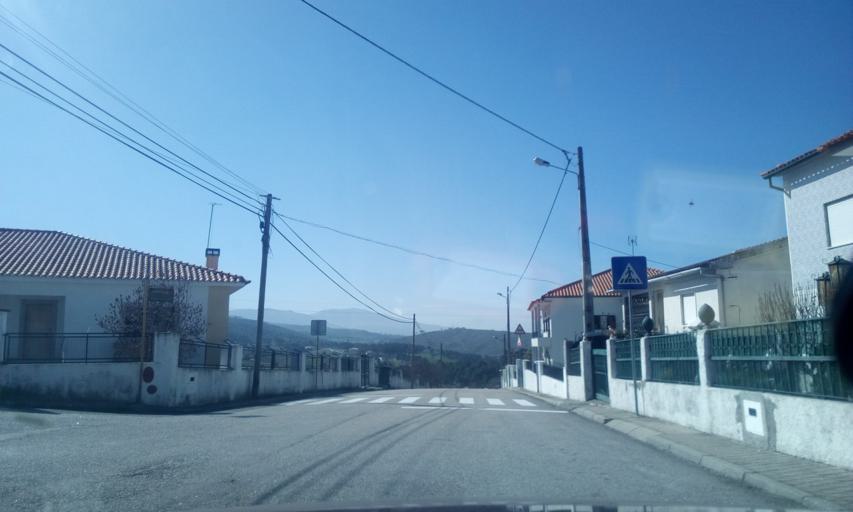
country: PT
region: Guarda
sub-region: Celorico da Beira
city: Celorico da Beira
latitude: 40.6215
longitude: -7.4069
